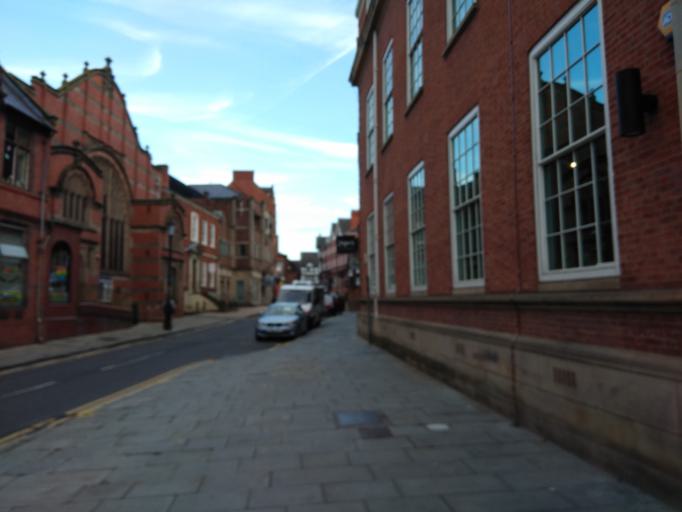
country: GB
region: England
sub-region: Cheshire West and Chester
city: Chester
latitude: 53.1896
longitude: -2.8877
